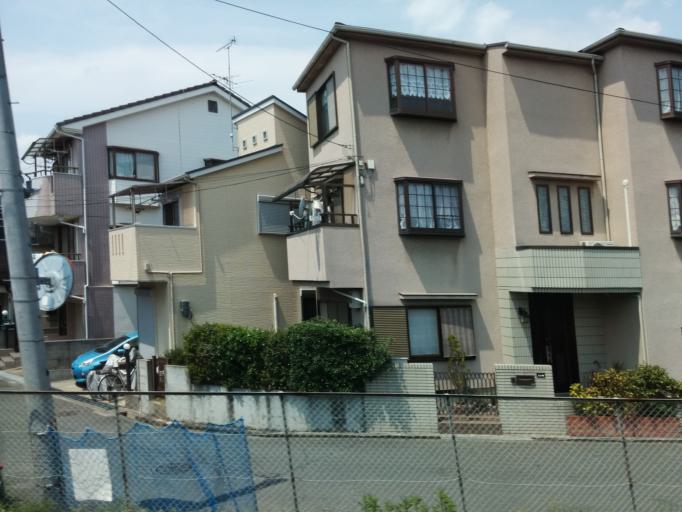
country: JP
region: Osaka
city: Ibaraki
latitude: 34.7950
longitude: 135.5599
